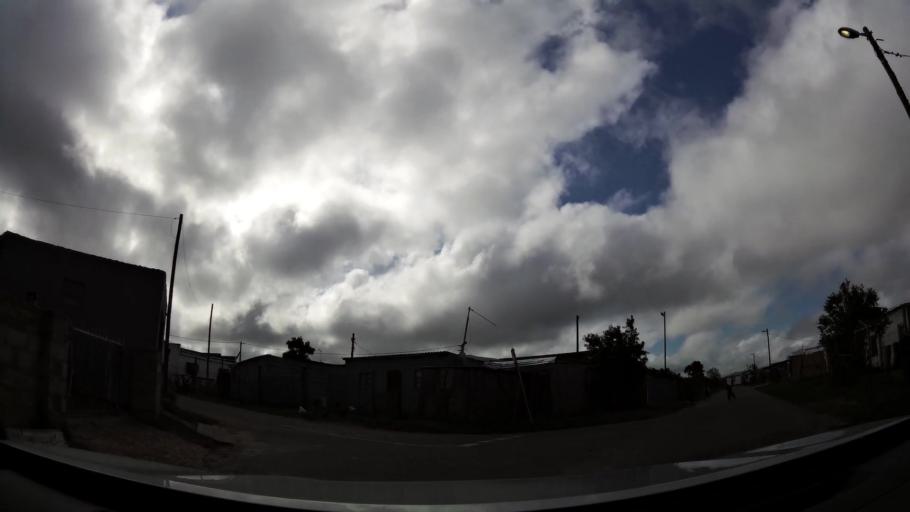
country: ZA
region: Western Cape
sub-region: Eden District Municipality
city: Plettenberg Bay
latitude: -34.0500
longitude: 23.3235
